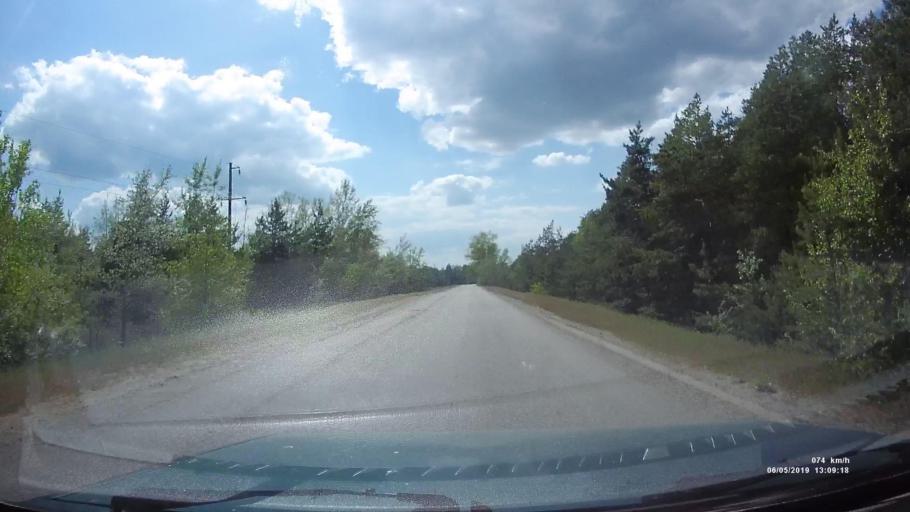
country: RU
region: Rostov
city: Ust'-Donetskiy
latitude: 47.7695
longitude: 40.9858
